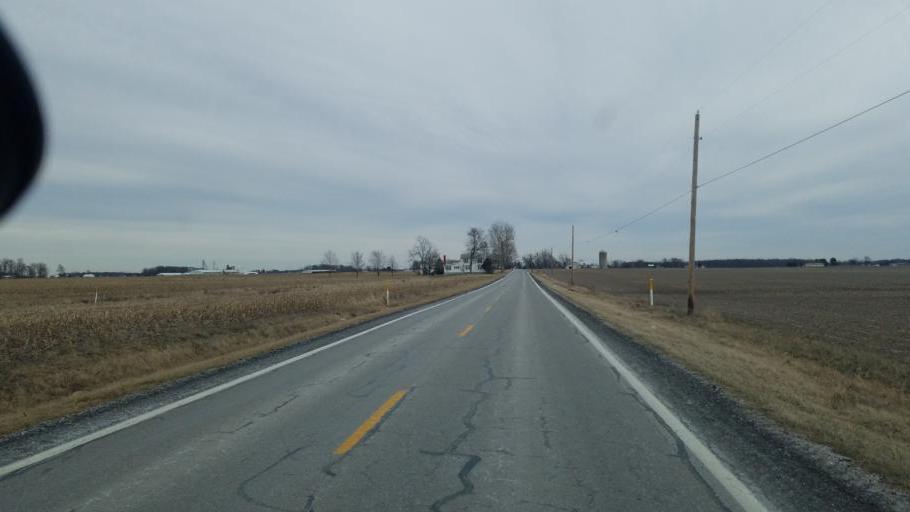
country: US
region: Ohio
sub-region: Marion County
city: Prospect
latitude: 40.4517
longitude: -83.1562
